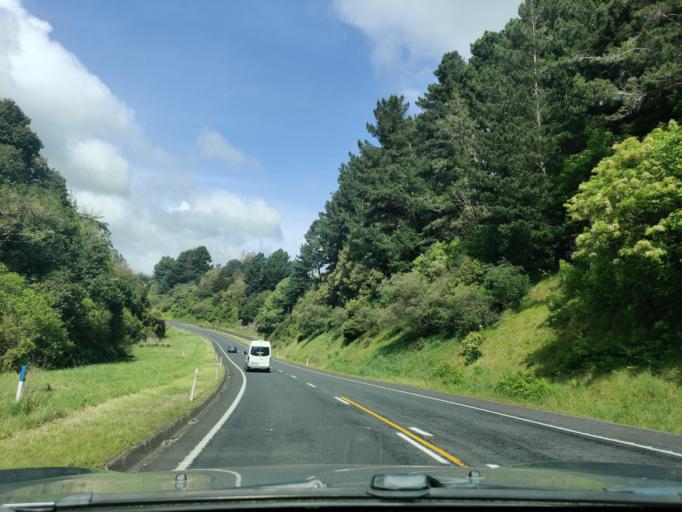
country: NZ
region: Manawatu-Wanganui
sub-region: Wanganui District
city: Wanganui
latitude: -39.8229
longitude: 174.8388
